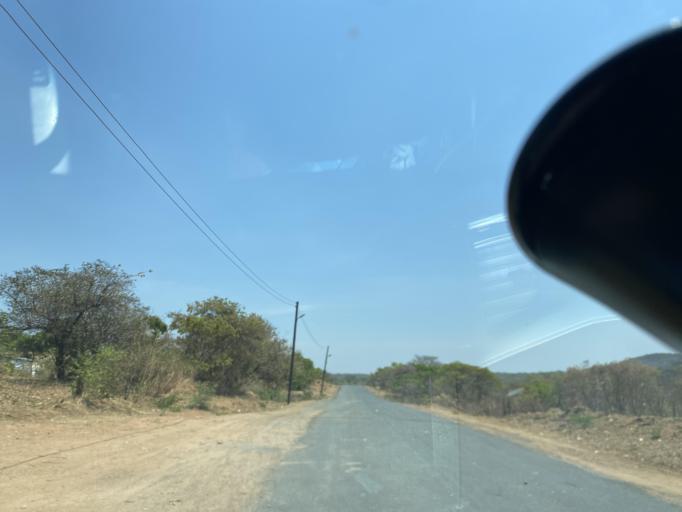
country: ZM
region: Lusaka
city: Kafue
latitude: -15.8676
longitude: 28.4341
